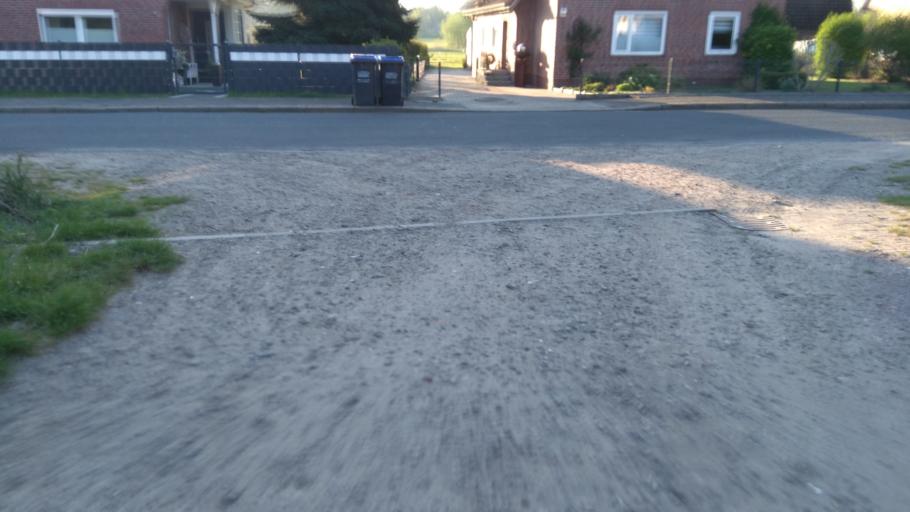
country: DE
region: Lower Saxony
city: Harsefeld
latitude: 53.4671
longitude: 9.5078
